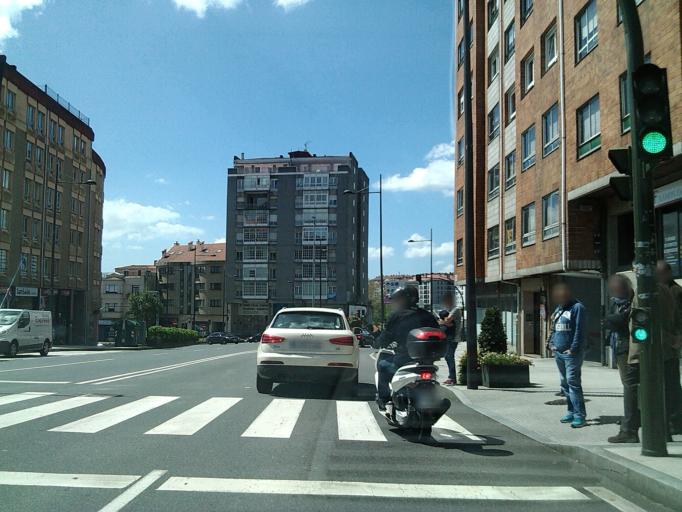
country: ES
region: Galicia
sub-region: Provincia da Coruna
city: Santiago de Compostela
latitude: 42.8700
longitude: -8.5475
